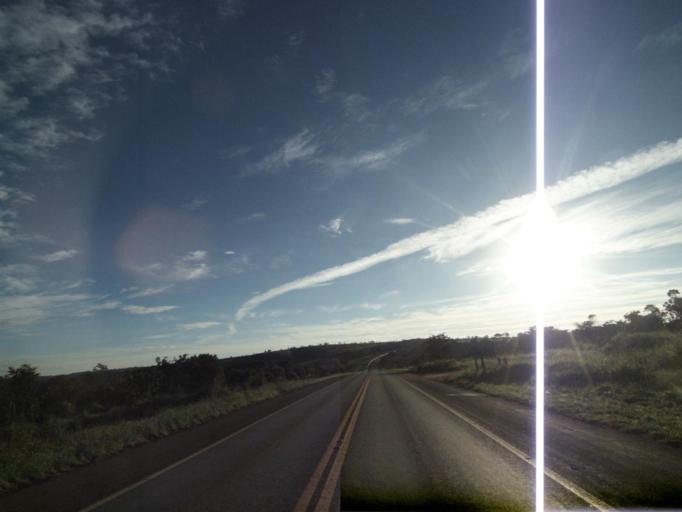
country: BR
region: Goias
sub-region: Pirenopolis
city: Pirenopolis
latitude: -15.7751
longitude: -48.5150
